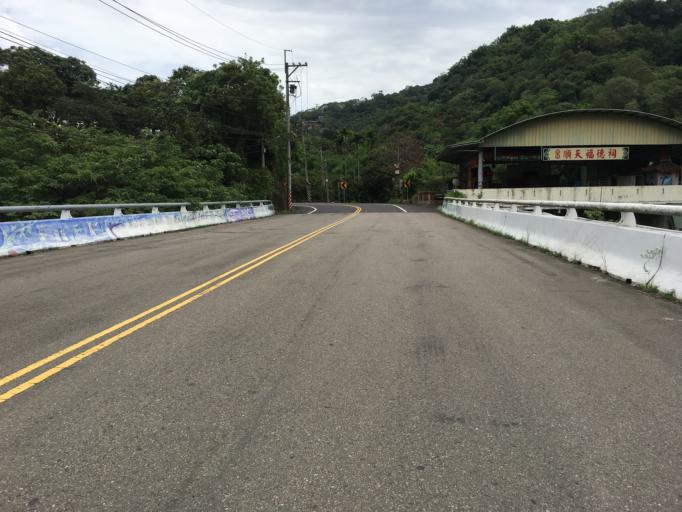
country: TW
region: Taiwan
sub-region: Taichung City
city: Taichung
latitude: 24.0715
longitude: 120.7326
